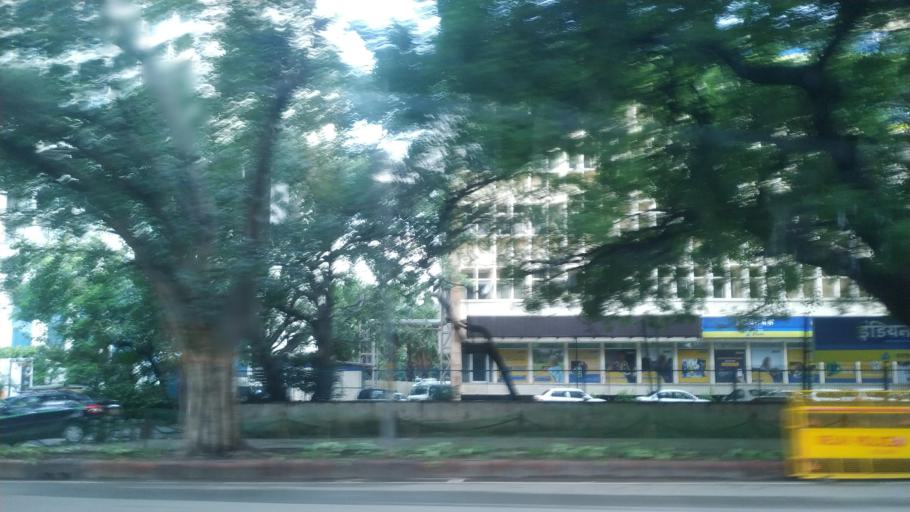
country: IN
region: NCT
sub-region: New Delhi
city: New Delhi
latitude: 28.6290
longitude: 77.2170
